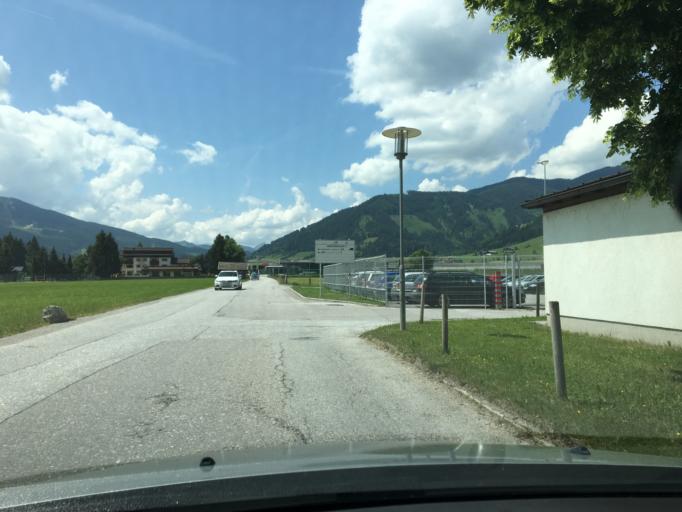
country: AT
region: Salzburg
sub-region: Politischer Bezirk Sankt Johann im Pongau
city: Altenmarkt im Pongau
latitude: 47.3839
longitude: 13.4072
